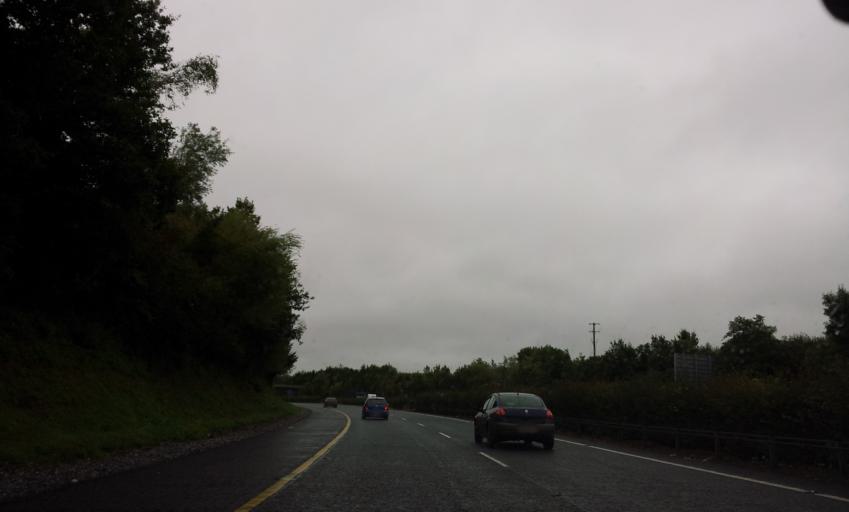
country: IE
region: Munster
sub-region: County Cork
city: Passage West
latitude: 51.9124
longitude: -8.3806
